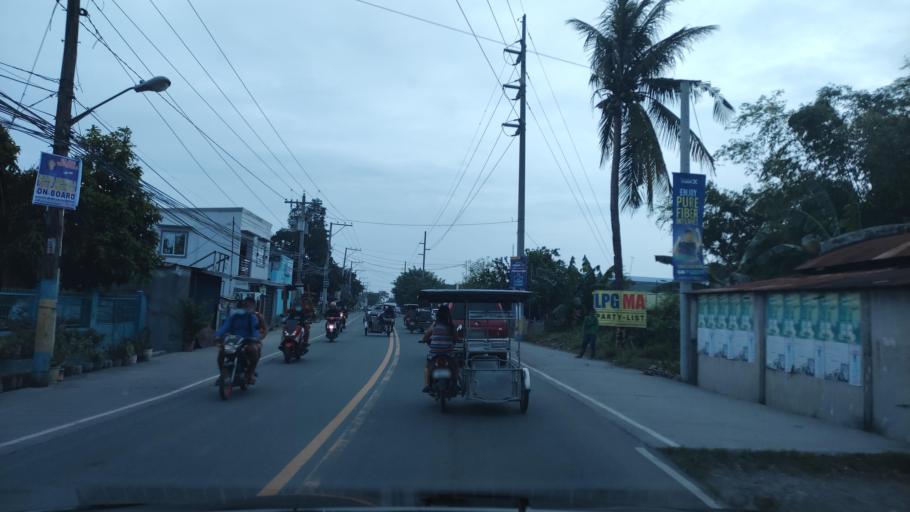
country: PH
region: Central Luzon
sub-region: Province of Pampanga
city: Santa Ana
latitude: 15.1027
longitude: 120.7705
